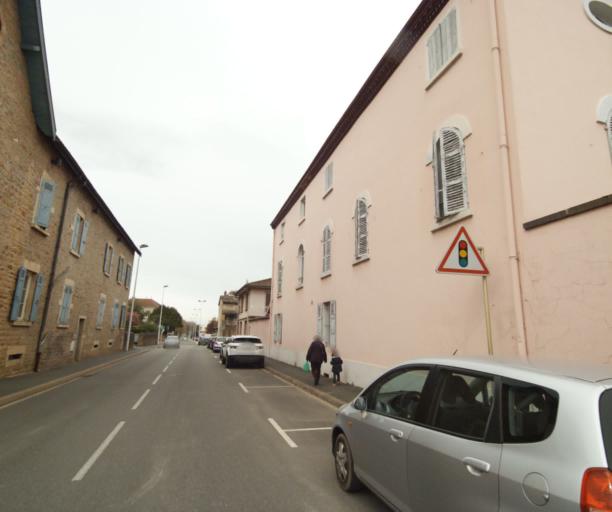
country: FR
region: Bourgogne
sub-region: Departement de Saone-et-Loire
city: Macon
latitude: 46.3068
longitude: 4.8203
